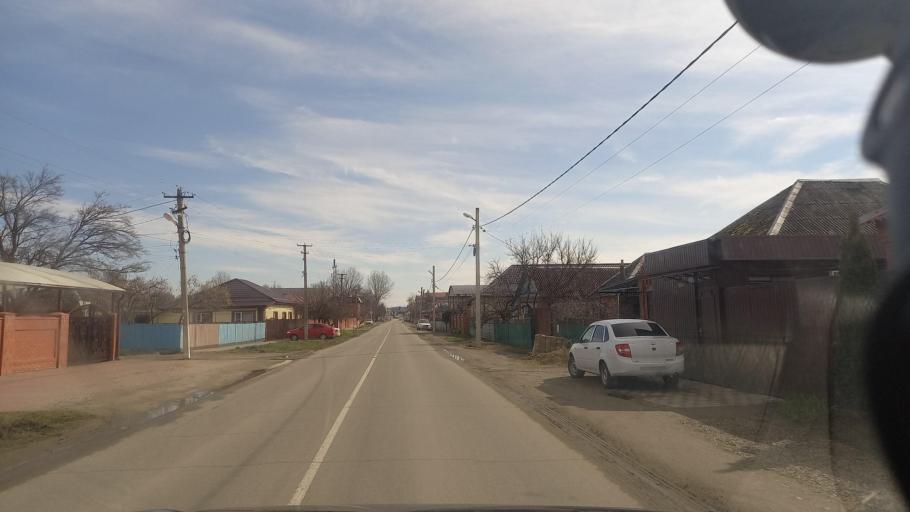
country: RU
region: Adygeya
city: Takhtamukay
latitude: 44.9265
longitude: 38.9858
